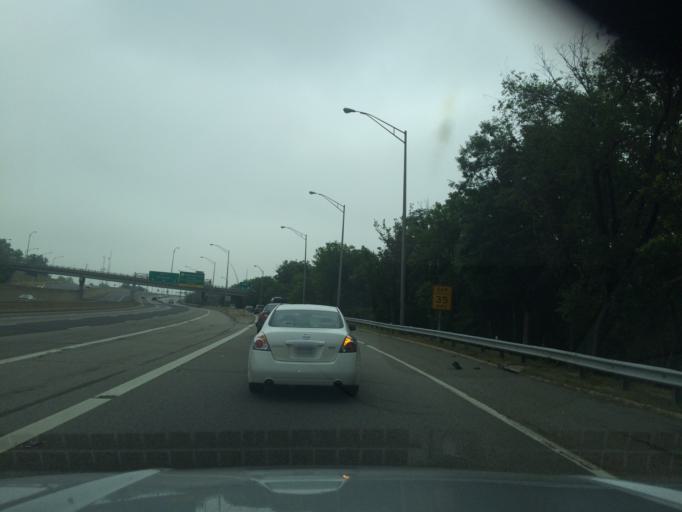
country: US
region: Virginia
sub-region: Arlington County
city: Arlington
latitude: 38.8597
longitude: -77.0695
